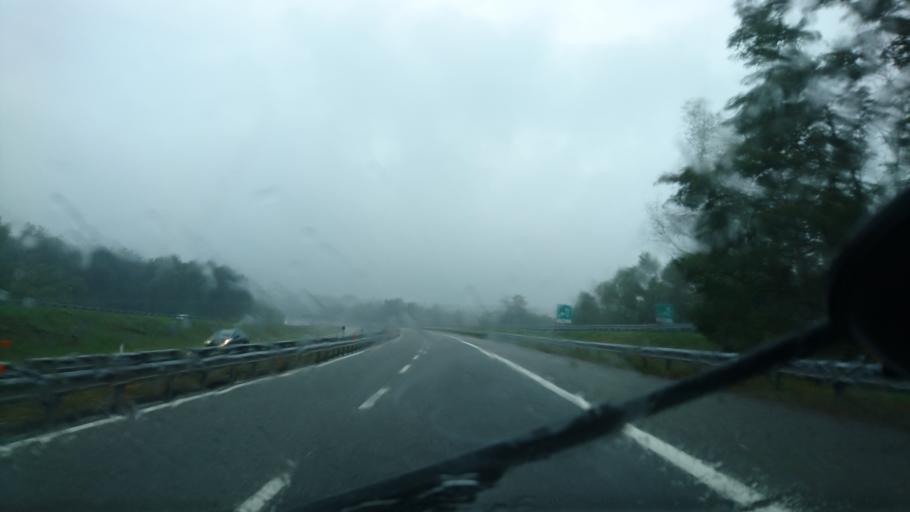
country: IT
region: Piedmont
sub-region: Provincia di Novara
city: Gattico
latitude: 45.7130
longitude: 8.5403
